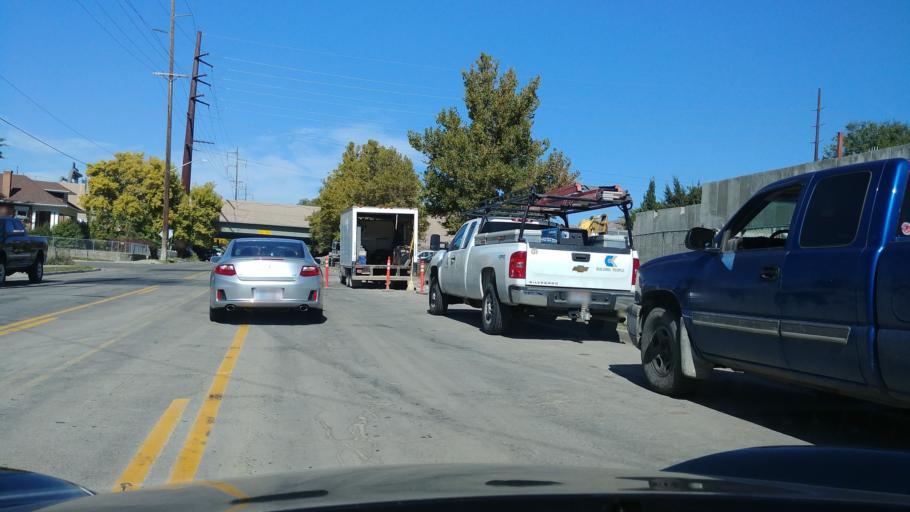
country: US
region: Utah
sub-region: Salt Lake County
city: South Salt Lake
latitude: 40.7179
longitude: -111.8654
